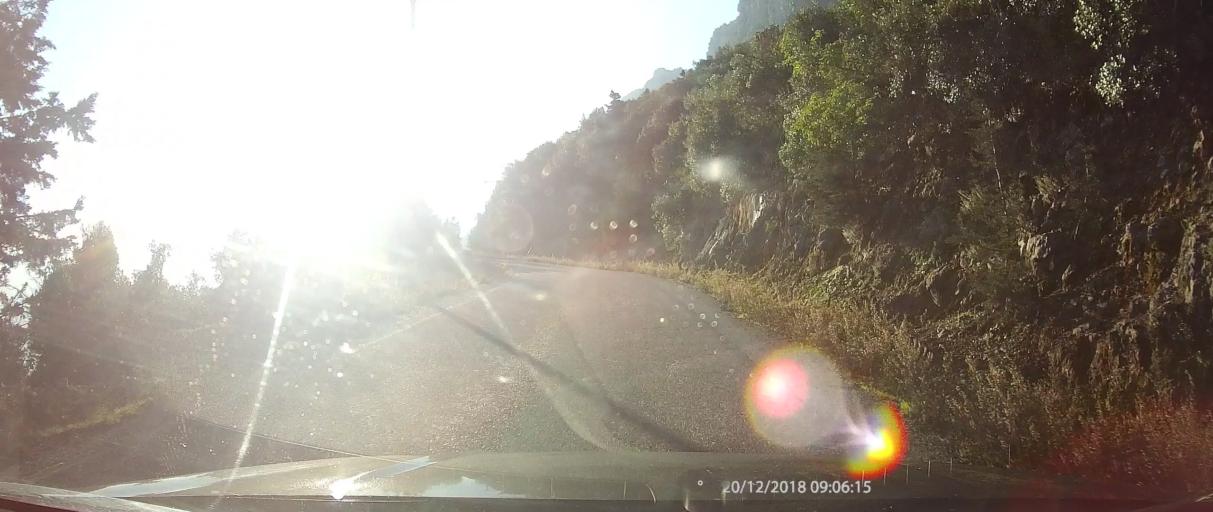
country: GR
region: Peloponnese
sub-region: Nomos Lakonias
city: Sykea
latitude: 36.9351
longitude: 22.9989
